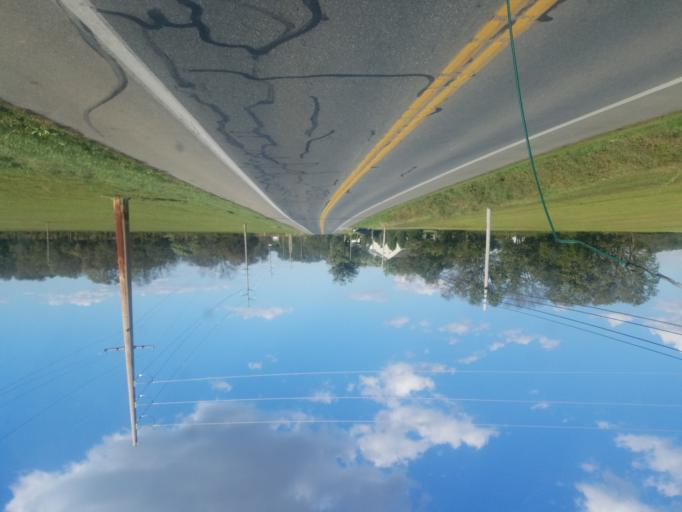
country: US
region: Pennsylvania
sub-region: Lancaster County
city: Bainbridge
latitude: 40.0781
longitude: -76.6518
